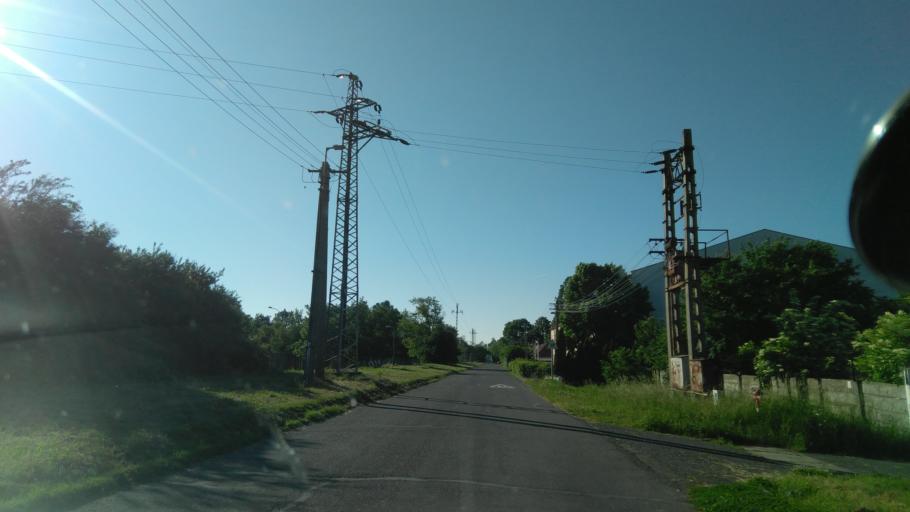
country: HU
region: Bekes
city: Gyula
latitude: 46.6375
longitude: 21.2567
